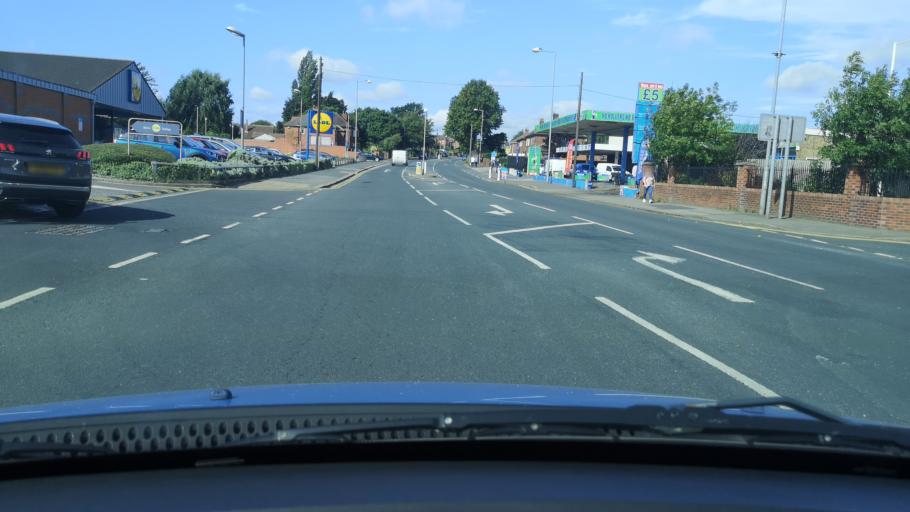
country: GB
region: England
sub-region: City and Borough of Wakefield
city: Ossett
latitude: 53.6806
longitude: -1.5809
